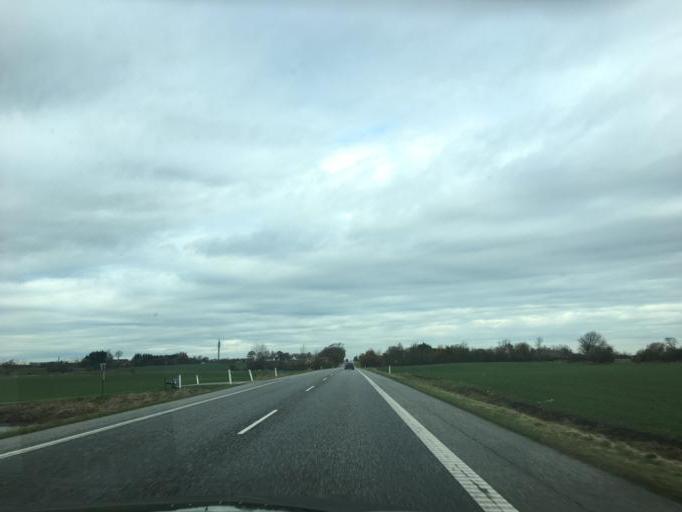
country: DK
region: South Denmark
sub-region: Vejle Kommune
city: Vejle
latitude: 55.6435
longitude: 9.4991
